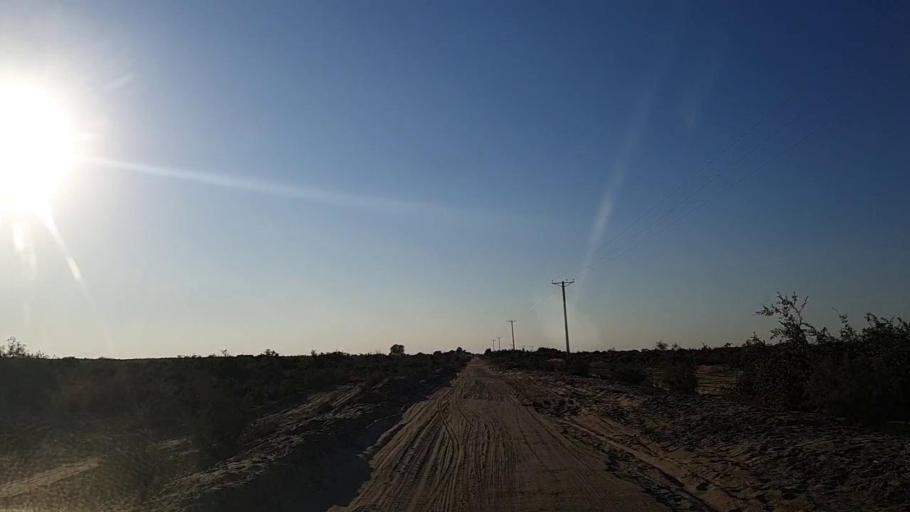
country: PK
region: Sindh
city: Khadro
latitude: 26.2790
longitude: 68.8731
